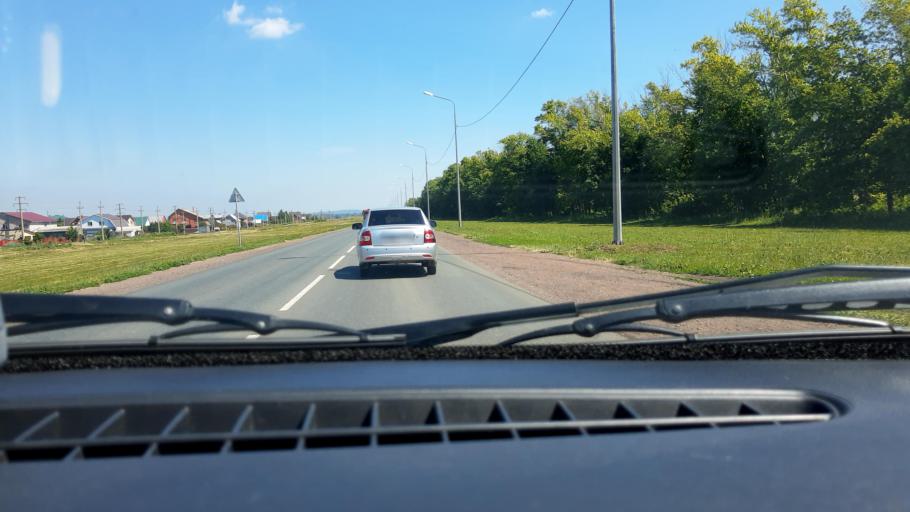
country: RU
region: Bashkortostan
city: Avdon
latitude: 54.4852
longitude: 55.8925
